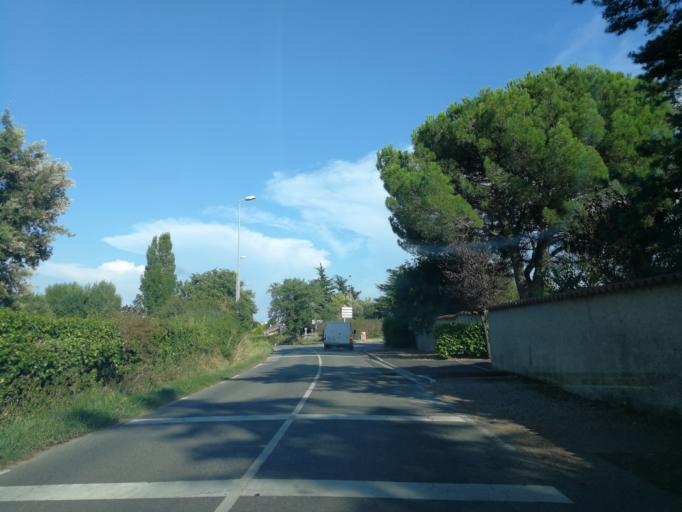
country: FR
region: Midi-Pyrenees
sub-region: Departement de la Haute-Garonne
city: Balma
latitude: 43.6210
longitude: 1.5131
